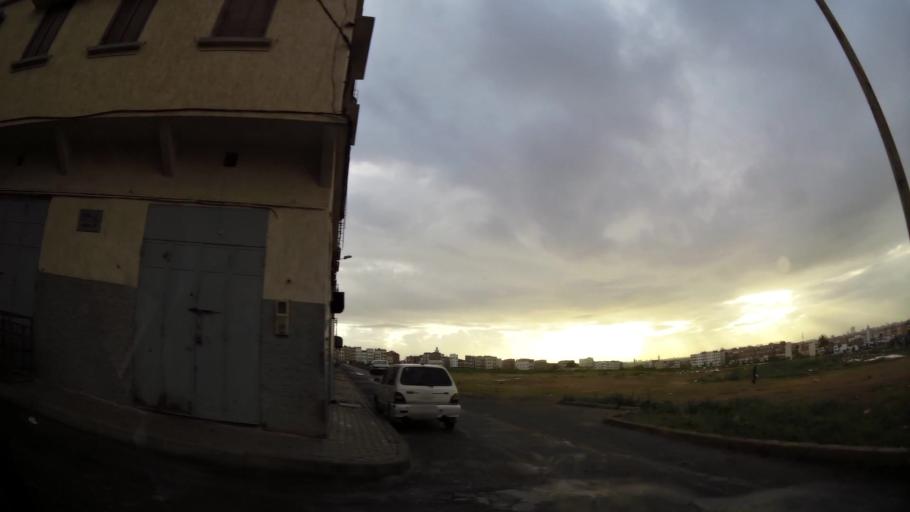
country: MA
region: Grand Casablanca
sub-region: Casablanca
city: Casablanca
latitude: 33.5566
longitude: -7.5749
